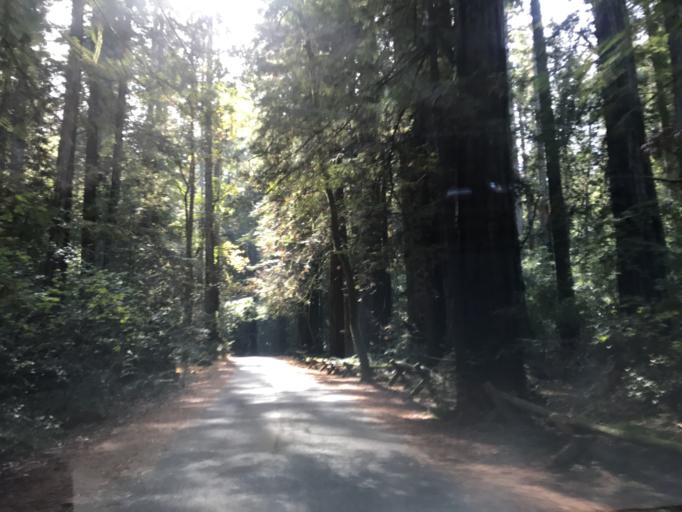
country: US
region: California
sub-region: Sonoma County
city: Guerneville
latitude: 38.5394
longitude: -123.0042
